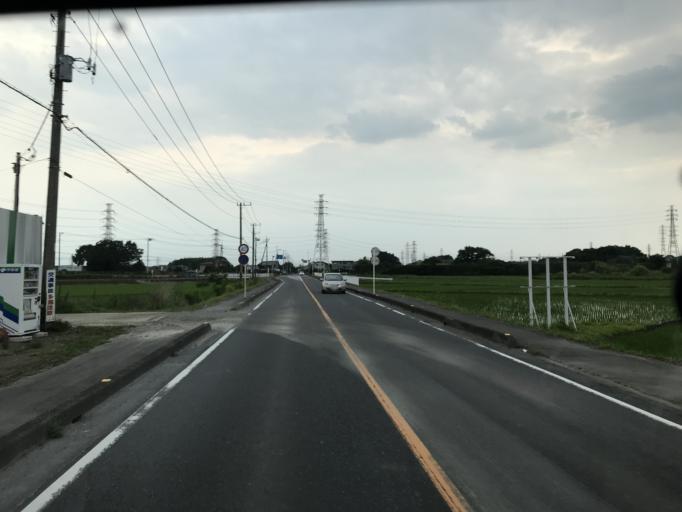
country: JP
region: Saitama
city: Shiraoka
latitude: 36.0123
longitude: 139.6872
